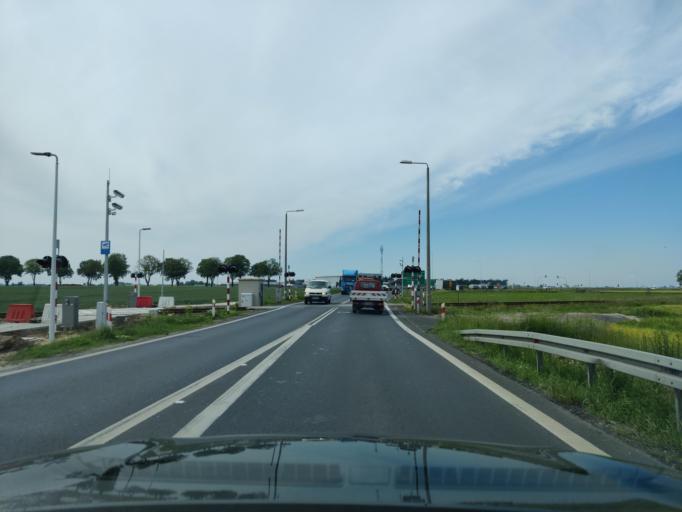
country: PL
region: Greater Poland Voivodeship
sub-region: Powiat grodziski
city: Granowo
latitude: 52.2226
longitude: 16.5844
